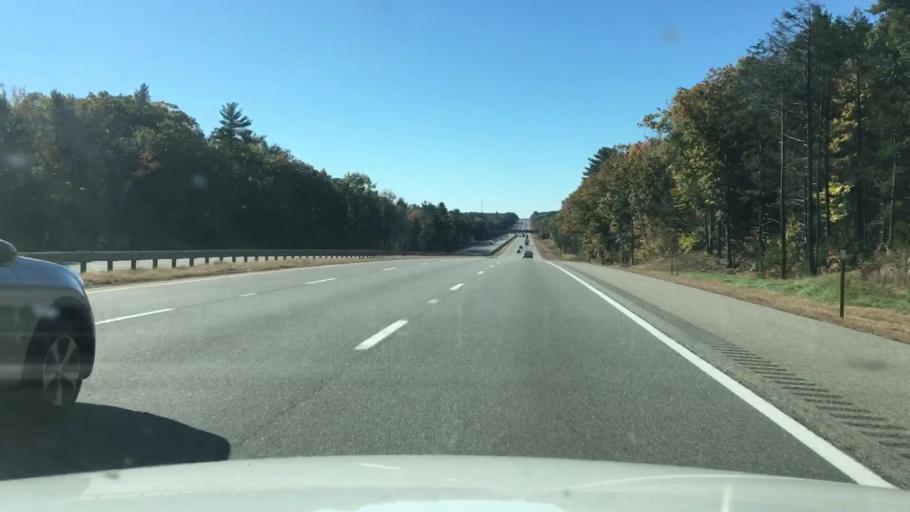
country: US
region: Maine
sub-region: York County
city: West Kennebunk
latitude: 43.3901
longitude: -70.5711
